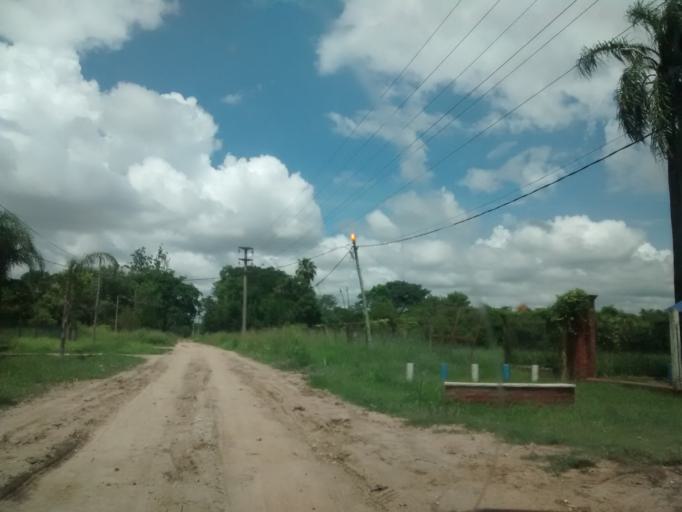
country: AR
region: Chaco
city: Fontana
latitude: -27.4102
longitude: -58.9841
